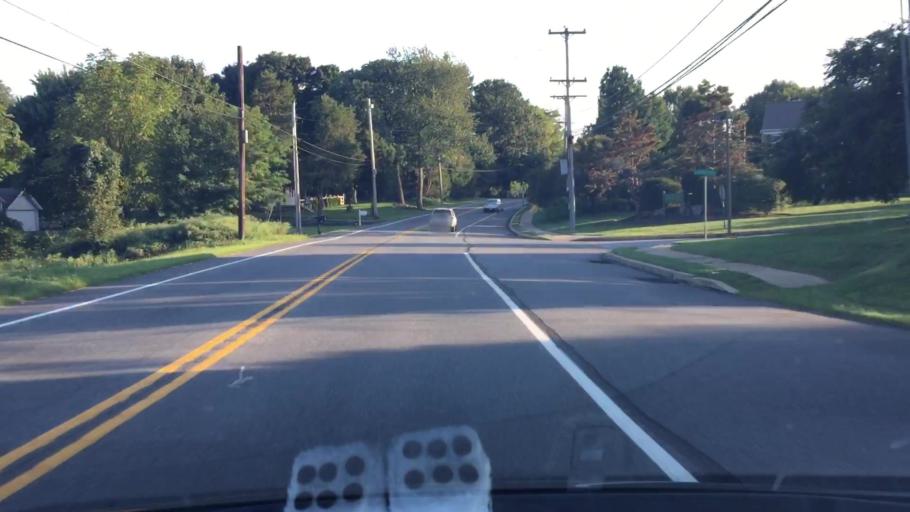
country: US
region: Pennsylvania
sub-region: Delaware County
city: Chester Heights
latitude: 39.8550
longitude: -75.4786
